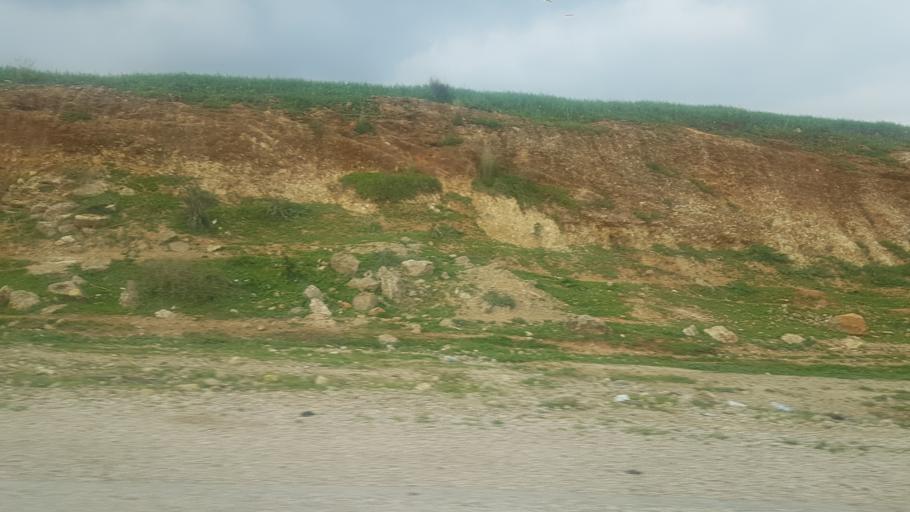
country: TR
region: Adana
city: Seyhan
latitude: 37.0554
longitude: 35.2202
